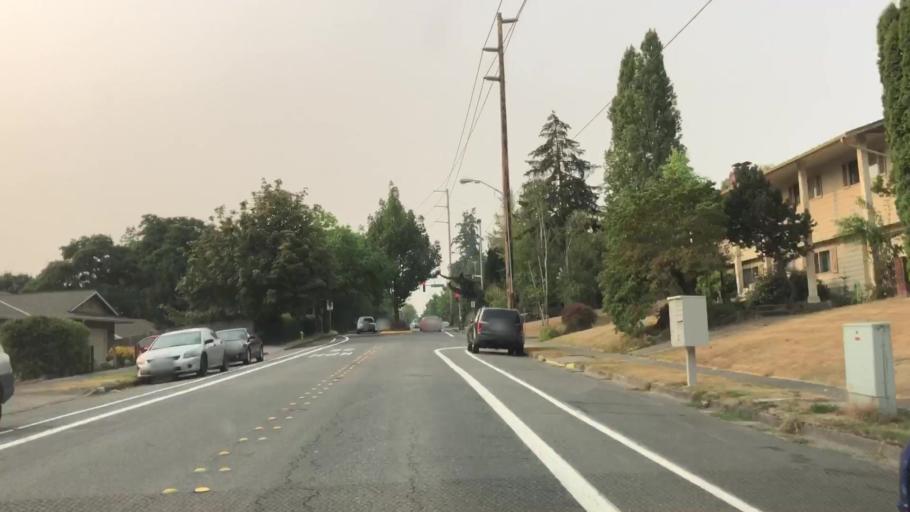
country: US
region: Washington
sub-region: King County
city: Redmond
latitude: 47.6552
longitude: -122.1325
